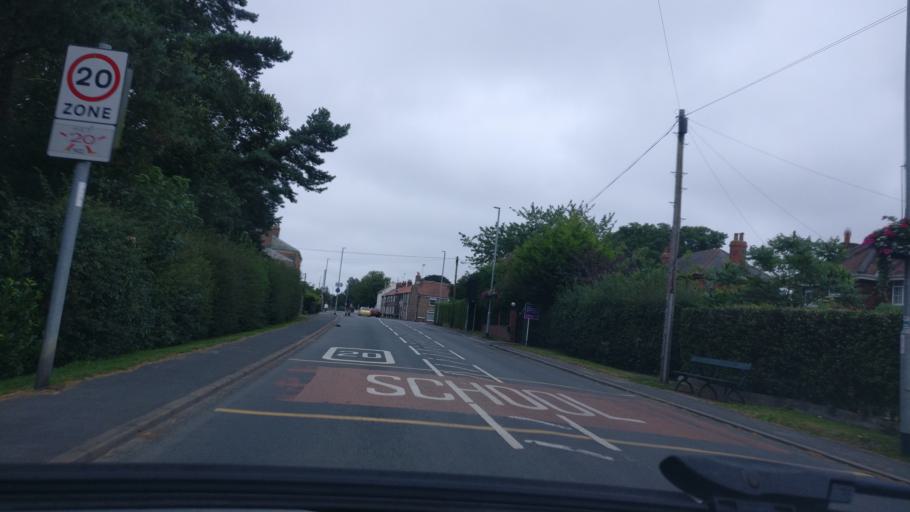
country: GB
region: England
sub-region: East Riding of Yorkshire
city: Leven
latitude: 53.8886
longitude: -0.3160
